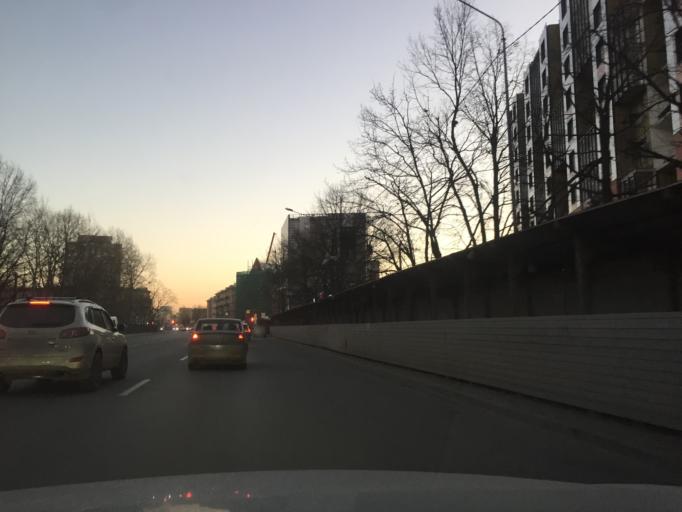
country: RU
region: St.-Petersburg
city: Obukhovo
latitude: 59.8827
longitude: 30.4346
